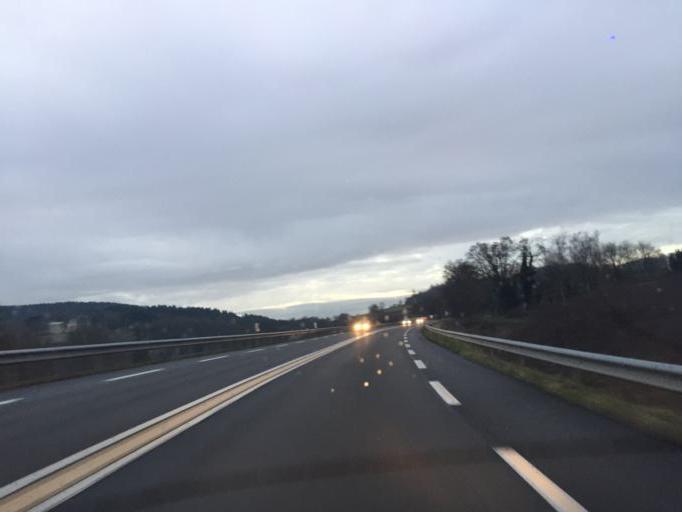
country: FR
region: Bourgogne
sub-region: Departement de Saone-et-Loire
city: Matour
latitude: 46.3656
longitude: 4.5654
